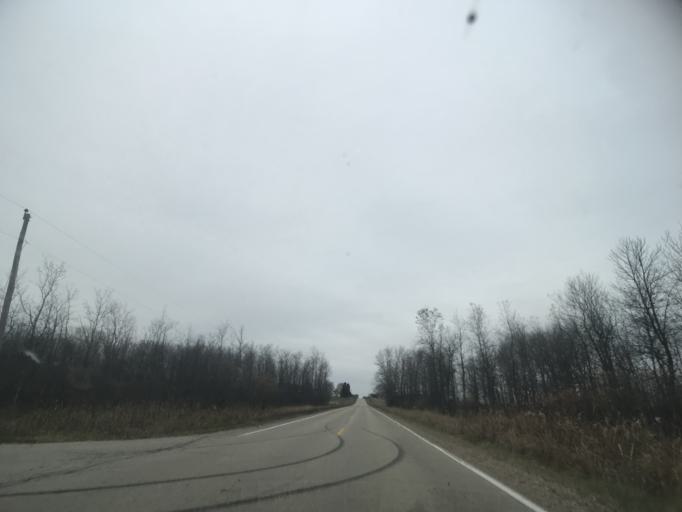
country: US
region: Wisconsin
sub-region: Oconto County
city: Gillett
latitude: 44.9835
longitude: -88.3058
